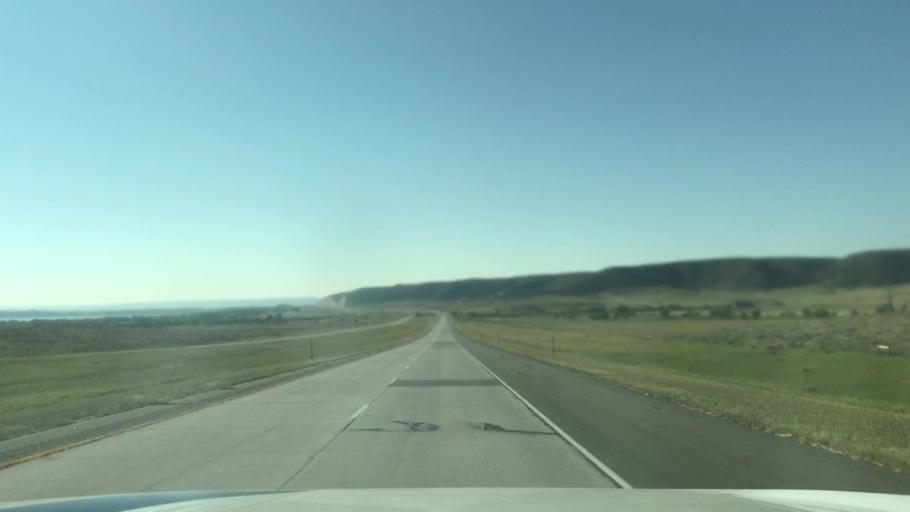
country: US
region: Wyoming
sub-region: Converse County
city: Douglas
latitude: 42.5852
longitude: -105.0844
